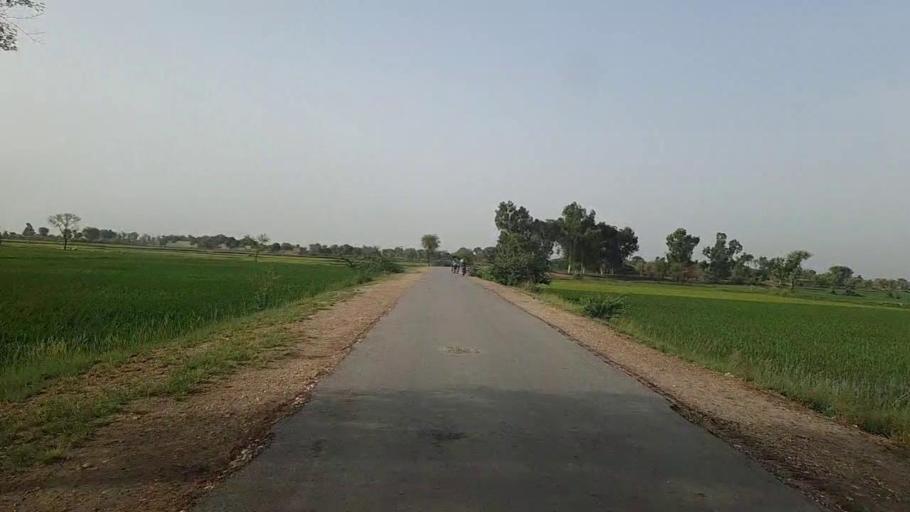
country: PK
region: Sindh
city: Khairpur Nathan Shah
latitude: 27.1227
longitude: 67.7895
